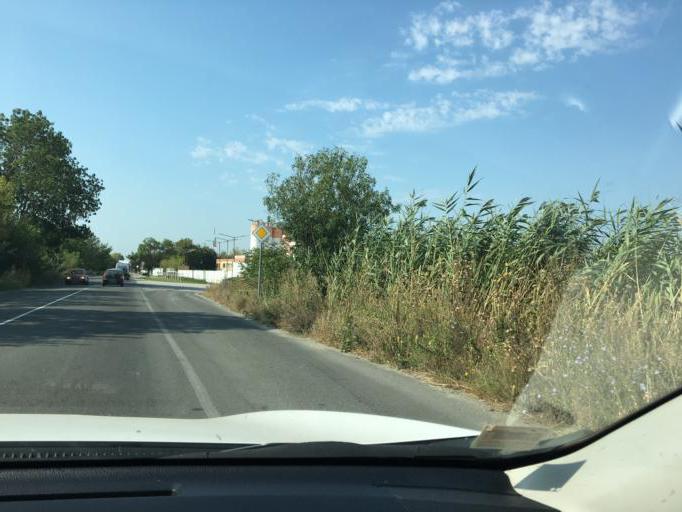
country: BG
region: Burgas
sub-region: Obshtina Burgas
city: Burgas
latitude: 42.5642
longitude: 27.4952
